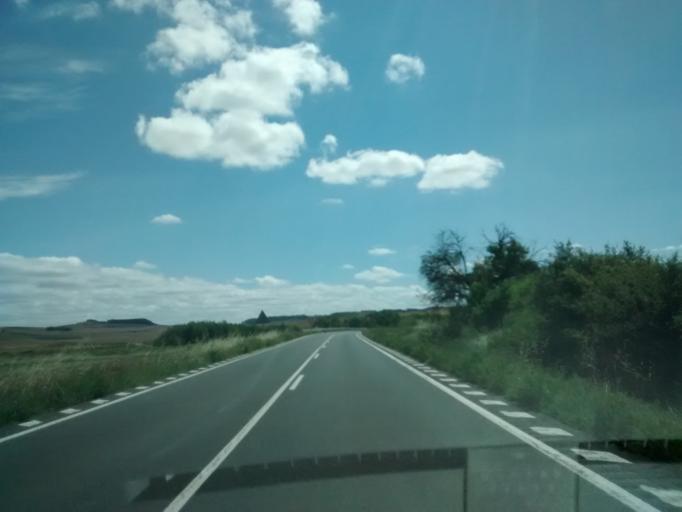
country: ES
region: La Rioja
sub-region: Provincia de La Rioja
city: Villamediana de Iregua
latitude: 42.4166
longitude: -2.3767
